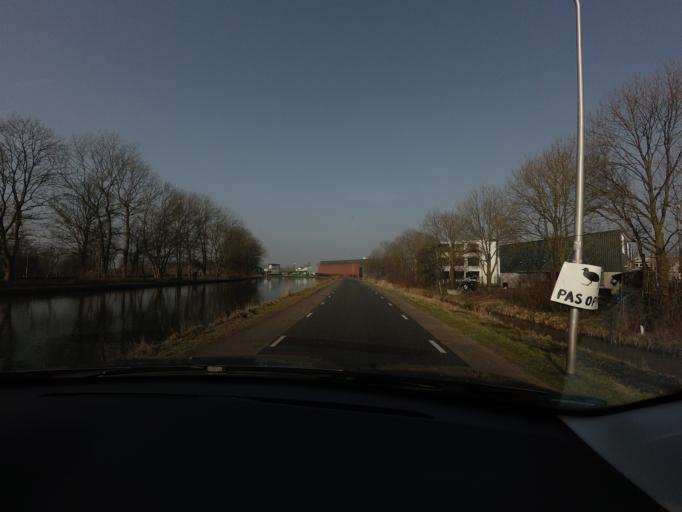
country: NL
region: North Holland
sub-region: Gemeente Diemen
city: Diemen
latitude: 52.3297
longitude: 4.9863
